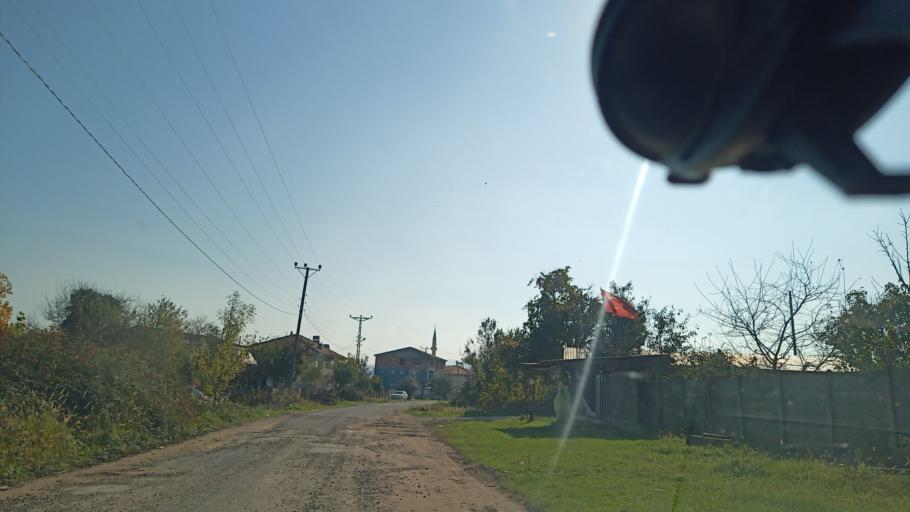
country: TR
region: Sakarya
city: Karasu
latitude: 41.0730
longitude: 30.8019
